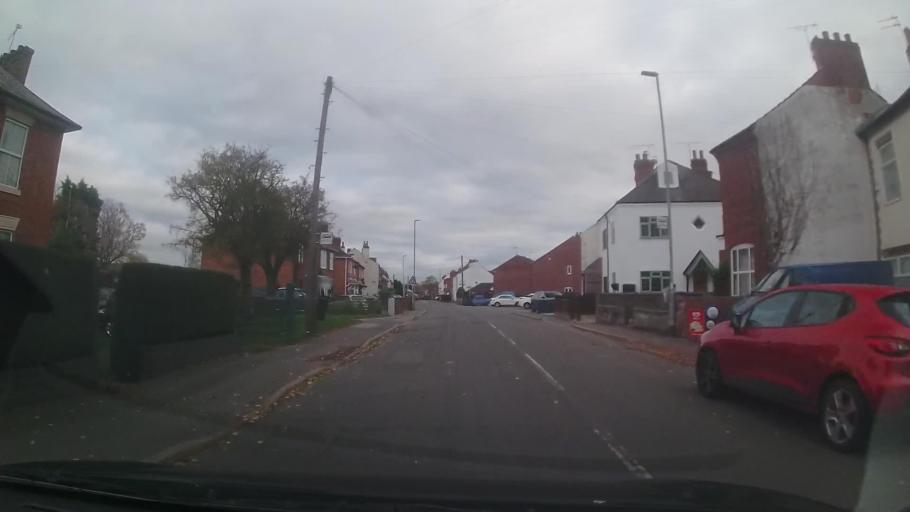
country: GB
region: England
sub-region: Leicestershire
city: Kirby Muxloe
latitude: 52.6450
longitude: -1.2407
